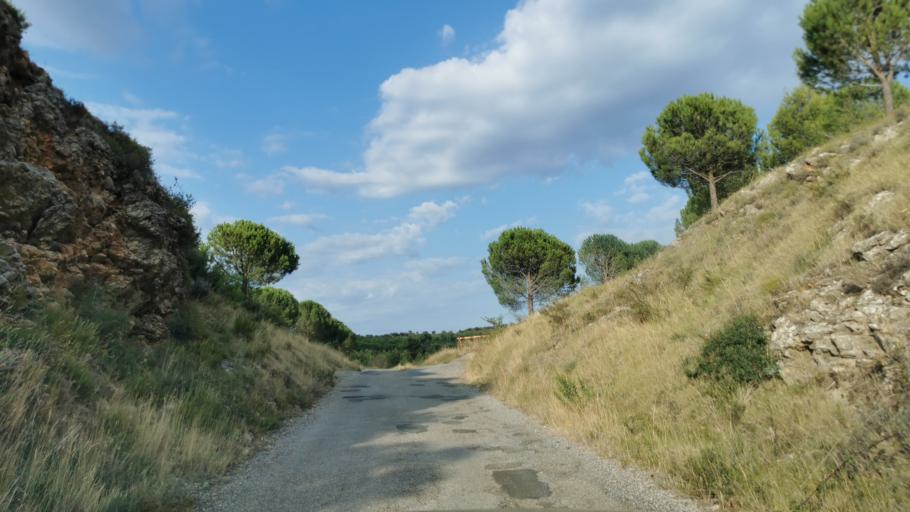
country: FR
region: Languedoc-Roussillon
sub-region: Departement de l'Aude
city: Bizanet
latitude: 43.1704
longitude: 2.8866
